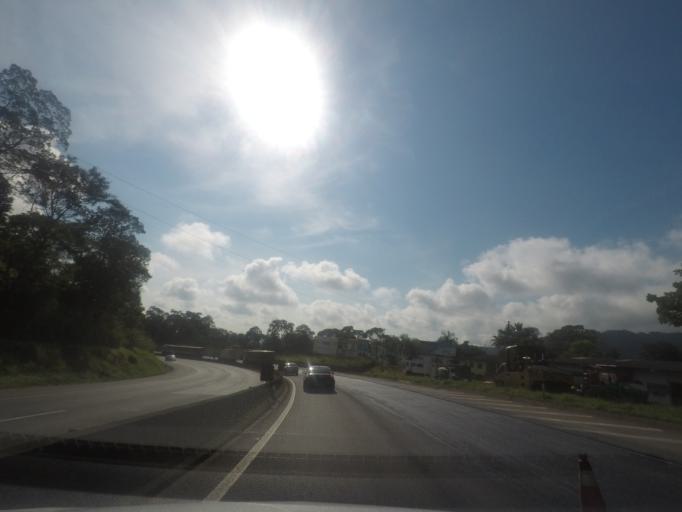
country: BR
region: Parana
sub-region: Antonina
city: Antonina
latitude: -25.5679
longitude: -48.8115
